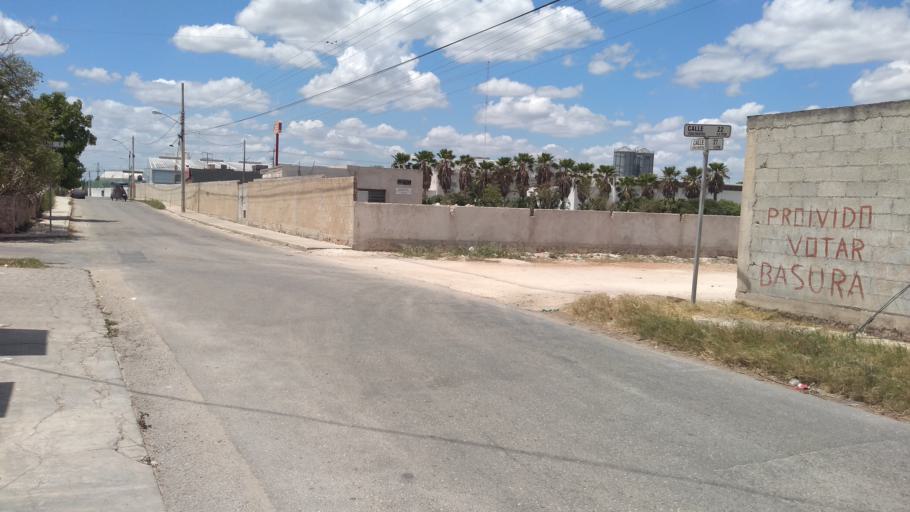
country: MX
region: Yucatan
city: Itzincab Palomeque
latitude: 20.9286
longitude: -89.6733
